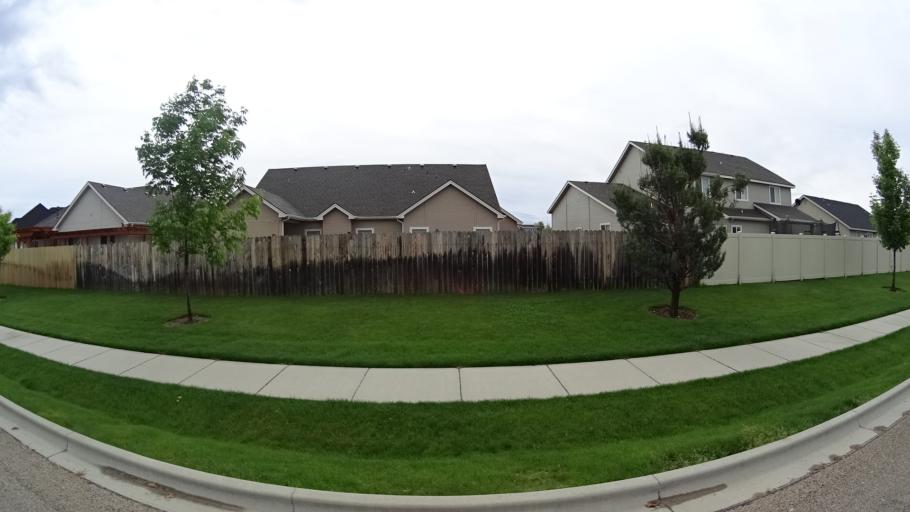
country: US
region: Idaho
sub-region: Ada County
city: Star
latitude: 43.6986
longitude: -116.5051
